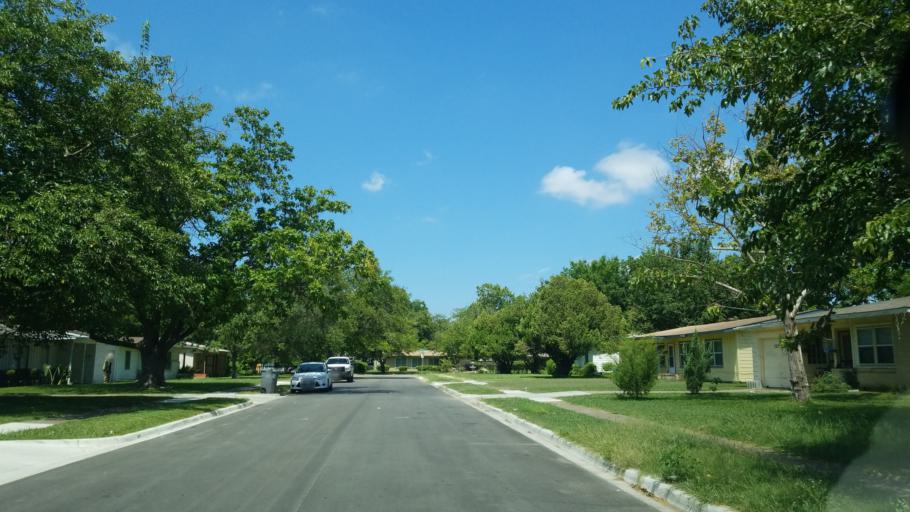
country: US
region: Texas
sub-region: Dallas County
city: Balch Springs
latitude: 32.7356
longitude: -96.6975
